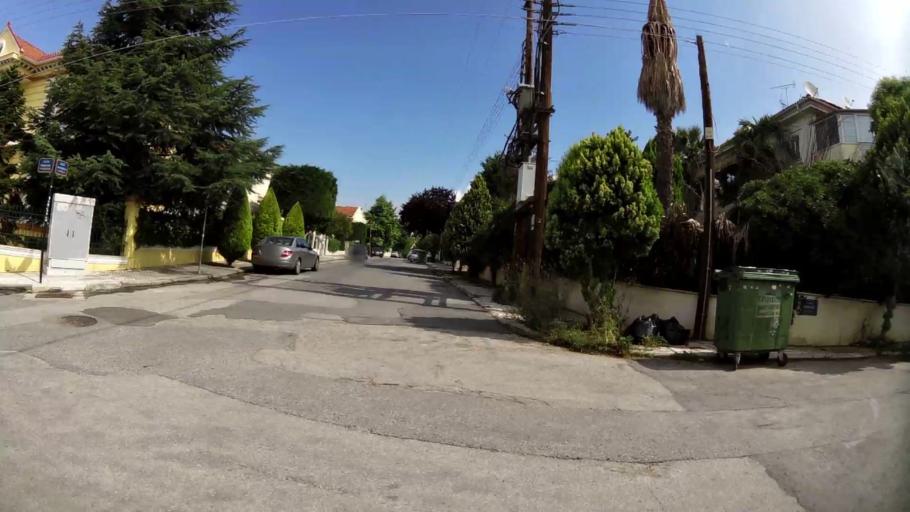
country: GR
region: Central Macedonia
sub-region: Nomos Thessalonikis
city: Panorama
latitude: 40.5836
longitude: 23.0153
